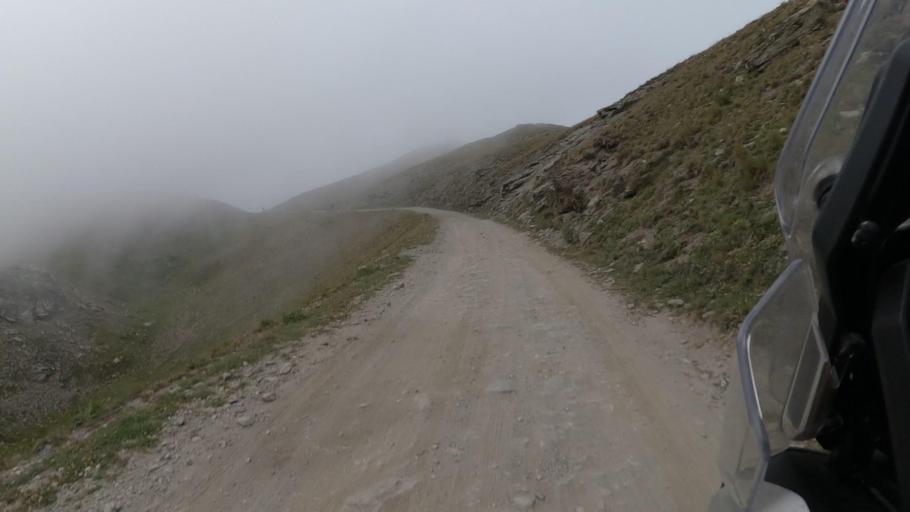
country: IT
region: Piedmont
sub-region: Provincia di Torino
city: Exilles
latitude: 45.0658
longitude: 6.9525
